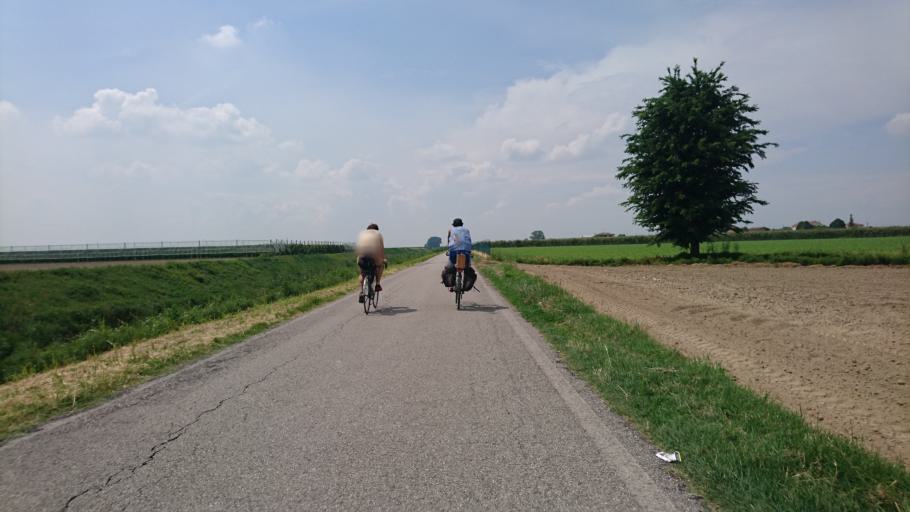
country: IT
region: Veneto
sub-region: Provincia di Rovigo
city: Giacciano con Baruchella
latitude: 45.0693
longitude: 11.4431
